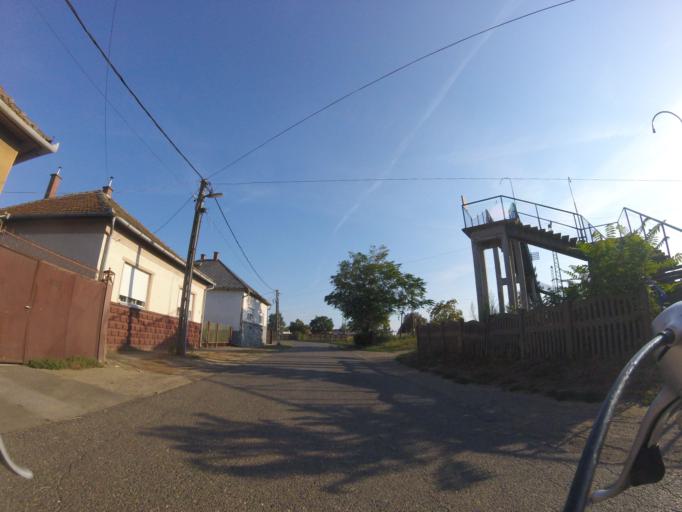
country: HU
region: Szabolcs-Szatmar-Bereg
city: Rakamaz
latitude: 48.1188
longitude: 21.4786
